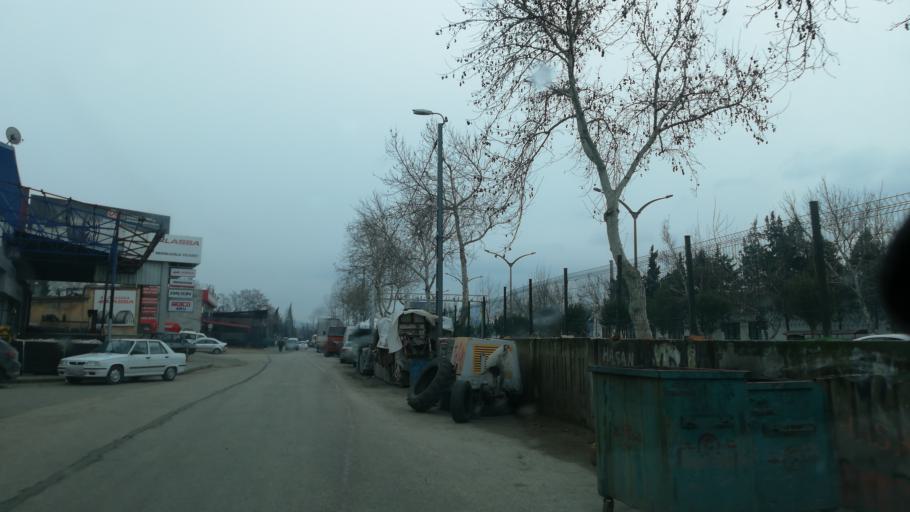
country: TR
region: Kahramanmaras
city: Kahramanmaras
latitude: 37.5602
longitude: 36.9556
